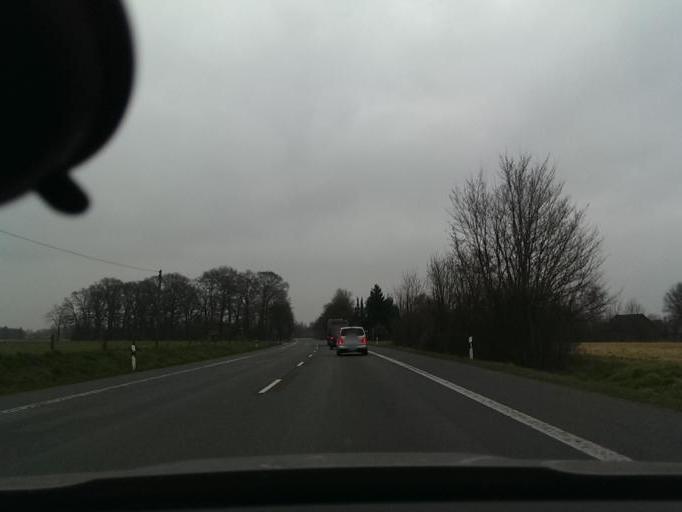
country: DE
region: North Rhine-Westphalia
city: Rietberg
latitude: 51.8210
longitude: 8.3867
